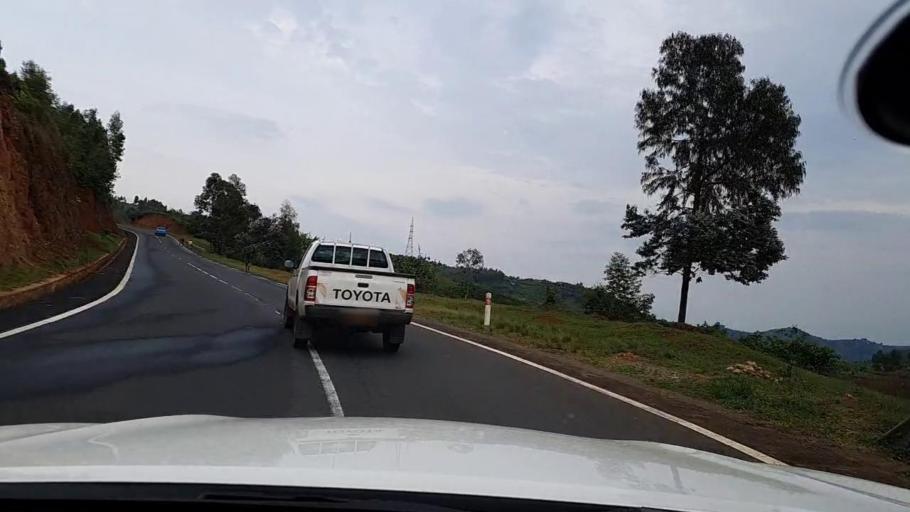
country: RW
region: Western Province
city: Kibuye
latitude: -2.1653
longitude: 29.2943
